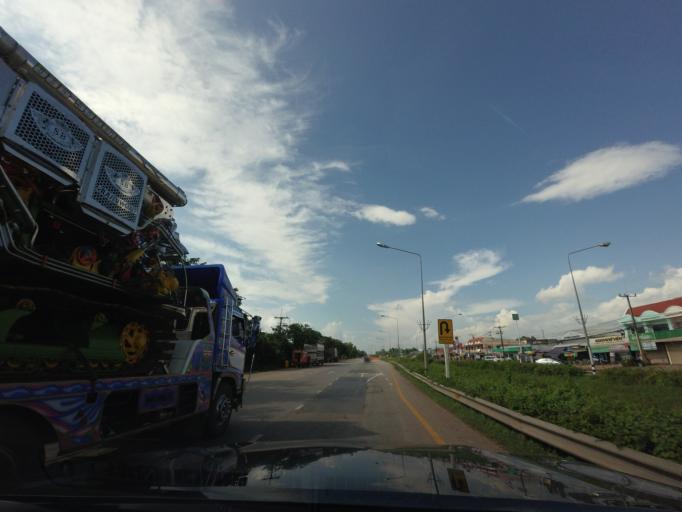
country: TH
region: Nong Khai
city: Sa Khrai
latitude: 17.6887
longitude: 102.7832
